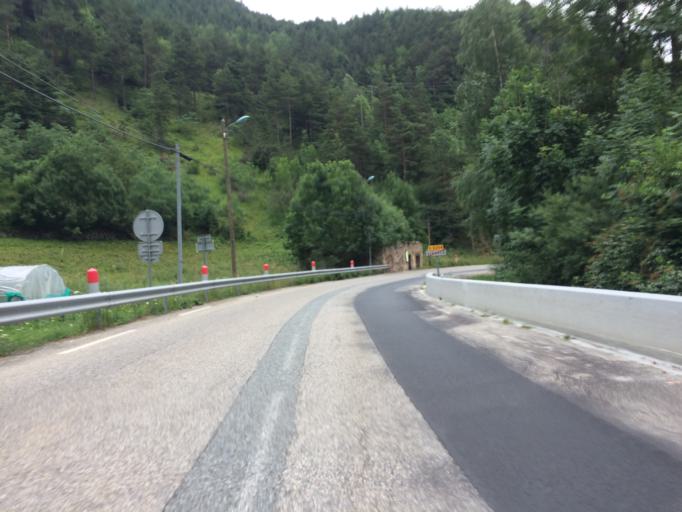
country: FR
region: Provence-Alpes-Cote d'Azur
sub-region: Departement des Alpes-Maritimes
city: Tende
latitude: 44.1100
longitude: 7.5685
